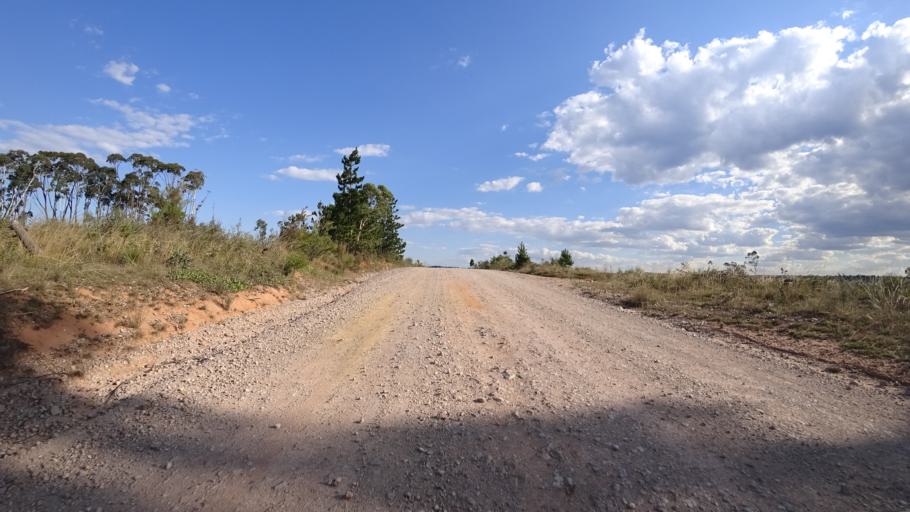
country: AU
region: New South Wales
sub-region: Lithgow
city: Lithgow
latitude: -33.3680
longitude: 150.2461
